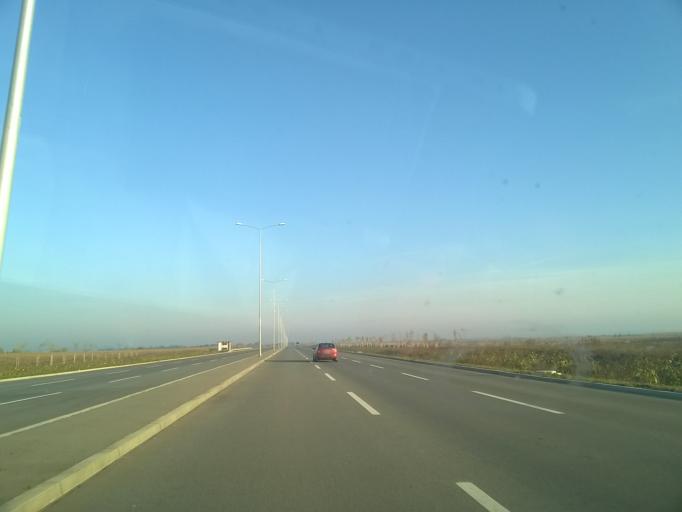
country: RS
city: Ovca
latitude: 44.8981
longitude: 20.5153
